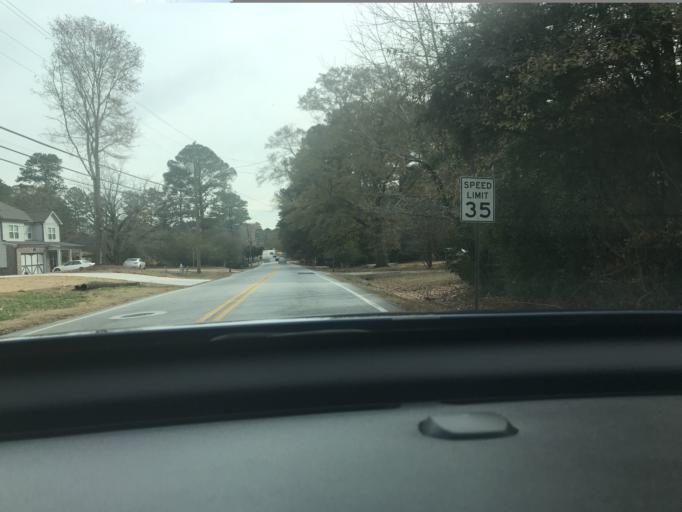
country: US
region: Georgia
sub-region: Gwinnett County
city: Lilburn
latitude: 33.9054
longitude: -84.1089
